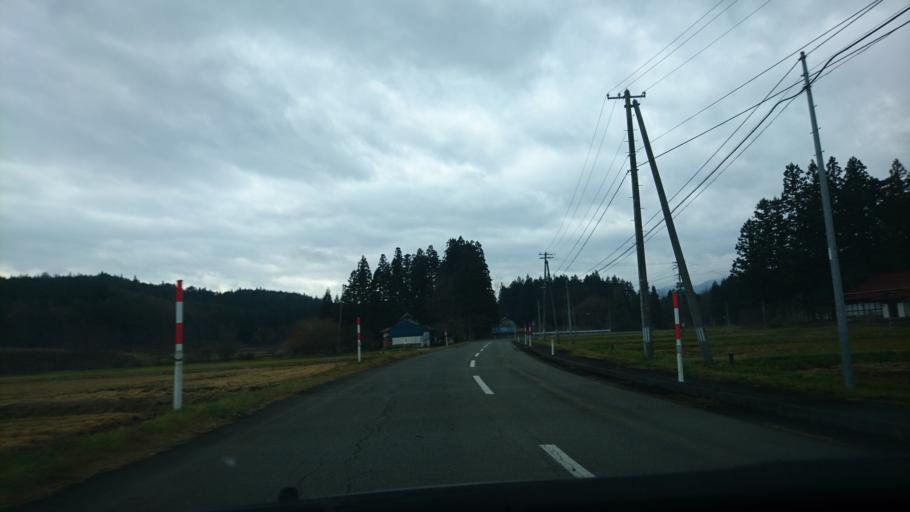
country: JP
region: Iwate
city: Ichinoseki
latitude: 38.9569
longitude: 140.9397
